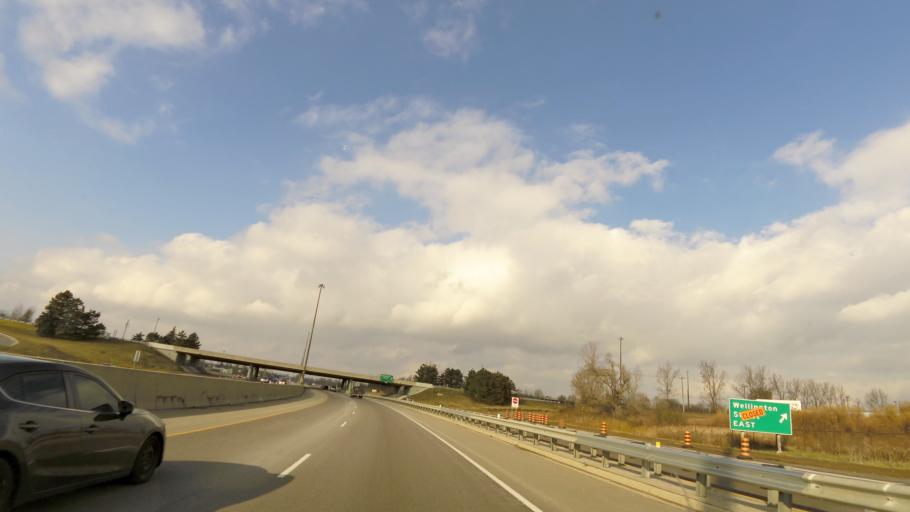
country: CA
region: Ontario
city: Waterloo
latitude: 43.4637
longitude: -80.4712
